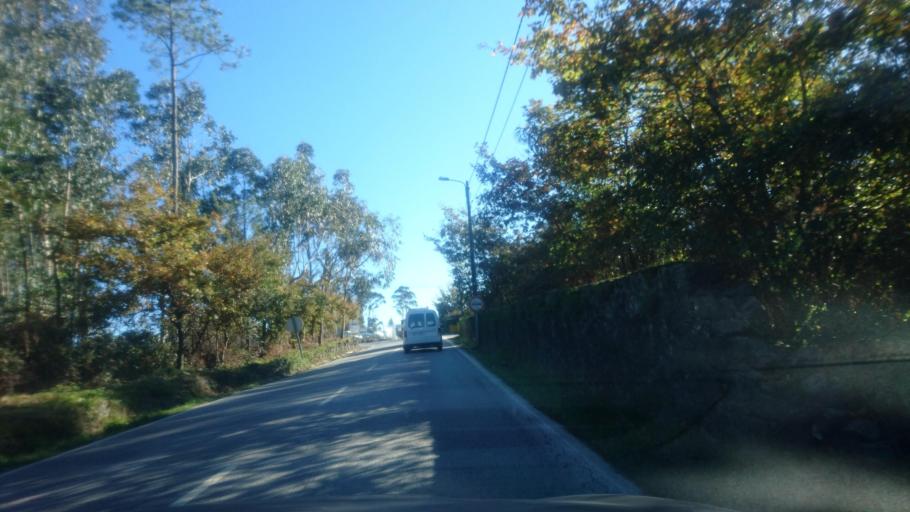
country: PT
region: Aveiro
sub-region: Vale de Cambra
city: Macieira de Cambra
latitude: 40.9017
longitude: -8.3831
